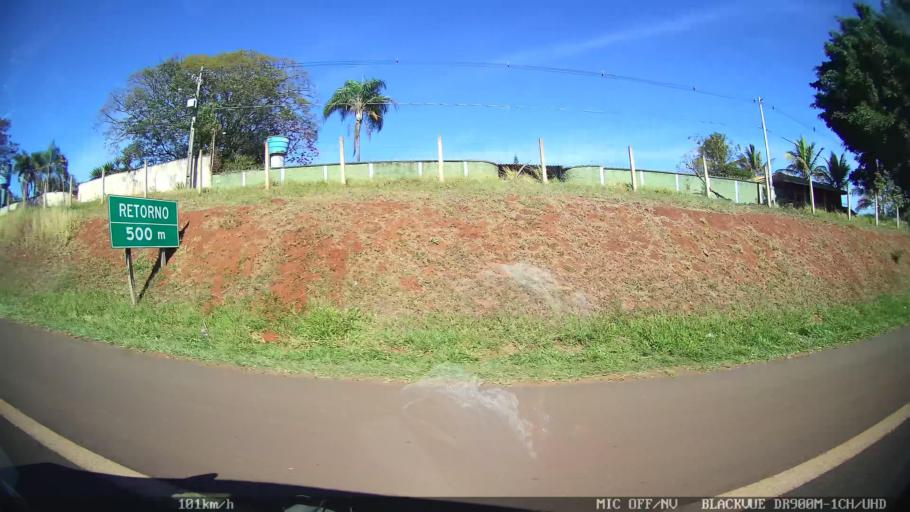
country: BR
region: Sao Paulo
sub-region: Franca
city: Franca
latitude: -20.5809
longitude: -47.3393
